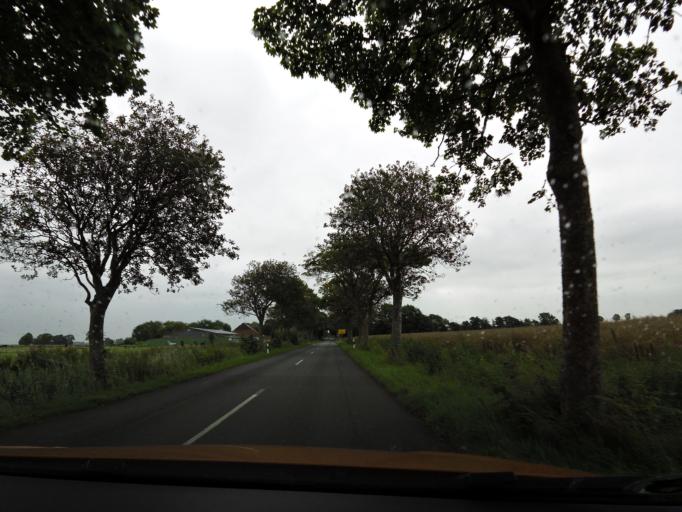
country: DE
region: Lower Saxony
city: Wirdum
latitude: 53.5039
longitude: 7.1946
